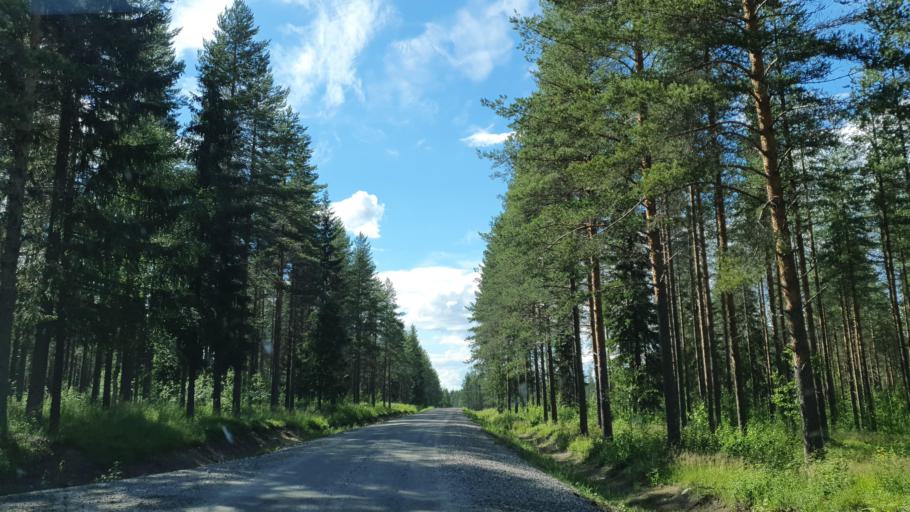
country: FI
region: Kainuu
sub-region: Kehys-Kainuu
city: Kuhmo
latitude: 64.1457
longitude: 29.7761
